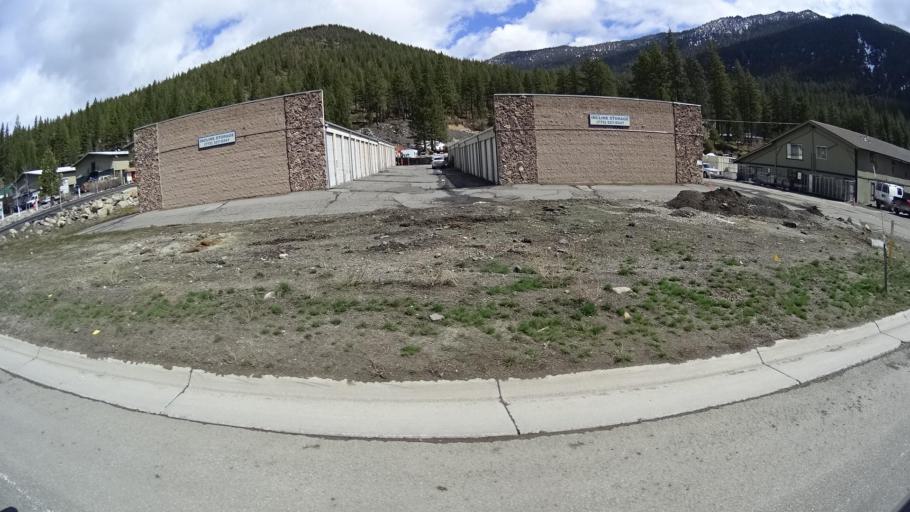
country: US
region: Nevada
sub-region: Washoe County
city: Incline Village
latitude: 39.2400
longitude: -119.9297
